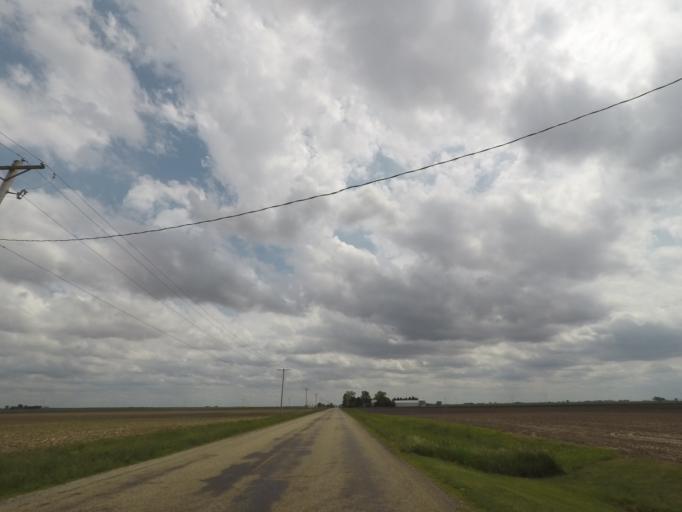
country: US
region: Illinois
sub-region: Macon County
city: Maroa
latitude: 40.0861
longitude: -89.0859
